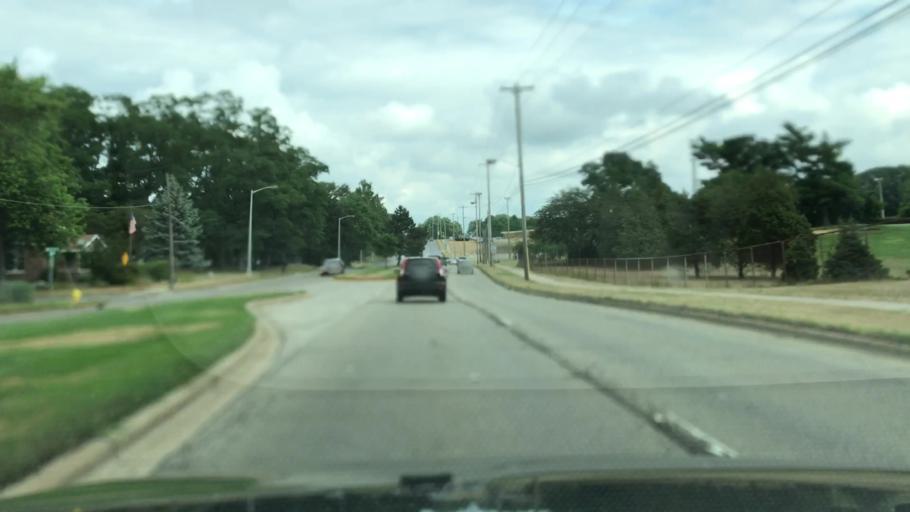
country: US
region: Michigan
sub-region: Kent County
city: Wyoming
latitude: 42.8843
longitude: -85.6981
